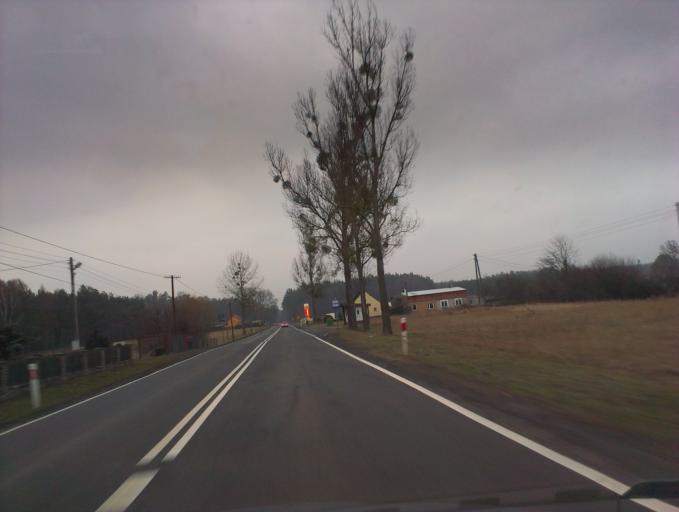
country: PL
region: Greater Poland Voivodeship
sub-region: Powiat zlotowski
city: Jastrowie
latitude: 53.3756
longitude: 16.7923
